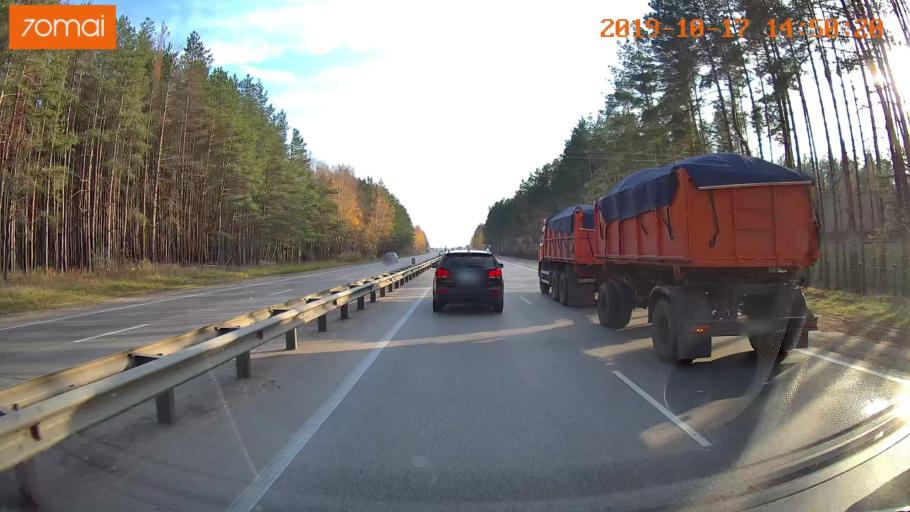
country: RU
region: Rjazan
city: Polyany
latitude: 54.7353
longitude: 39.8418
